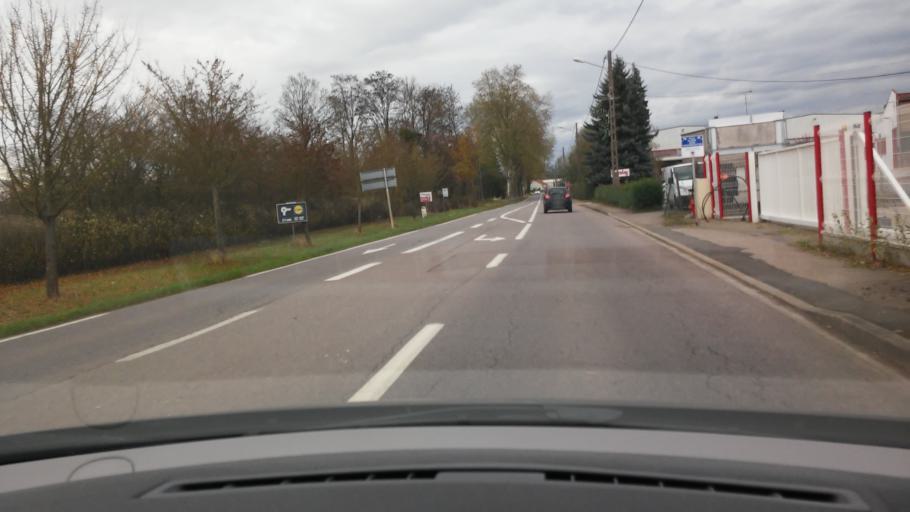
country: FR
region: Lorraine
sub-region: Departement de la Moselle
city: Boulay-Moselle
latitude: 49.1806
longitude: 6.4792
